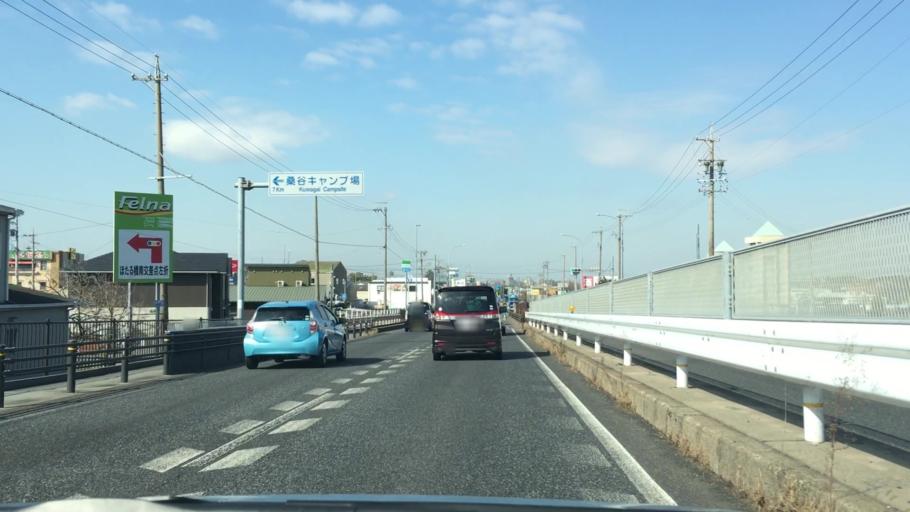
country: JP
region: Aichi
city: Okazaki
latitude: 34.9247
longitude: 137.2024
